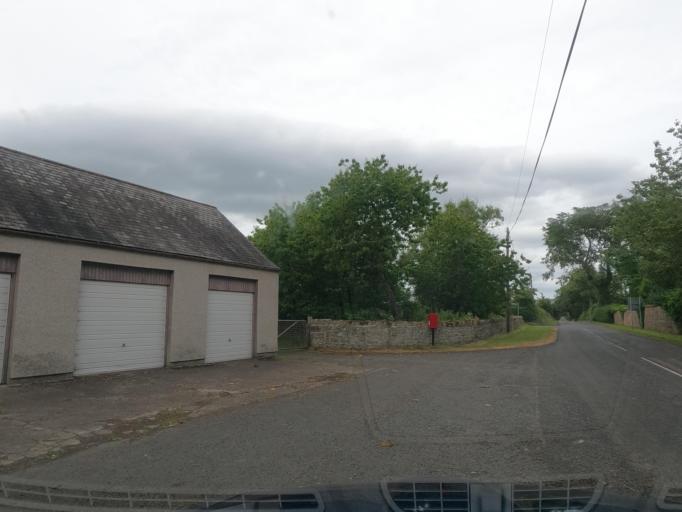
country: GB
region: England
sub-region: Northumberland
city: Doddington
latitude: 55.5600
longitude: -1.9361
